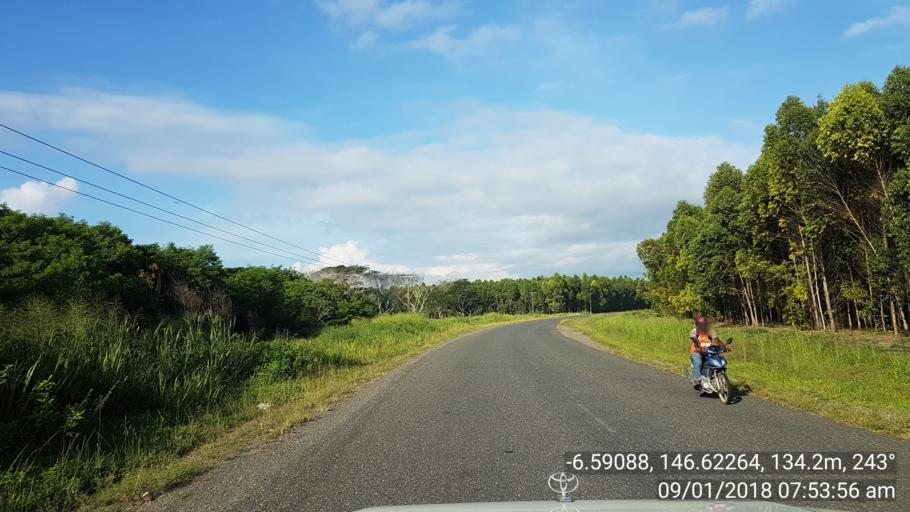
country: PG
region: Morobe
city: Lae
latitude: -6.5905
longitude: 146.6231
